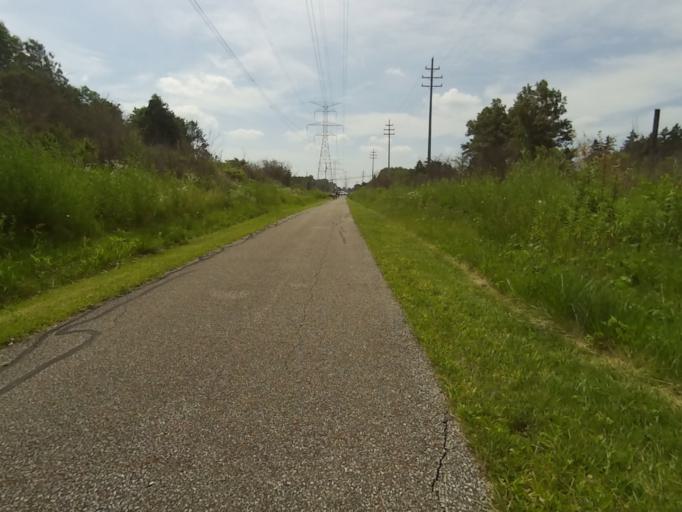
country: US
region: Ohio
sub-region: Summit County
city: Northfield
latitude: 41.3157
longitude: -81.5643
